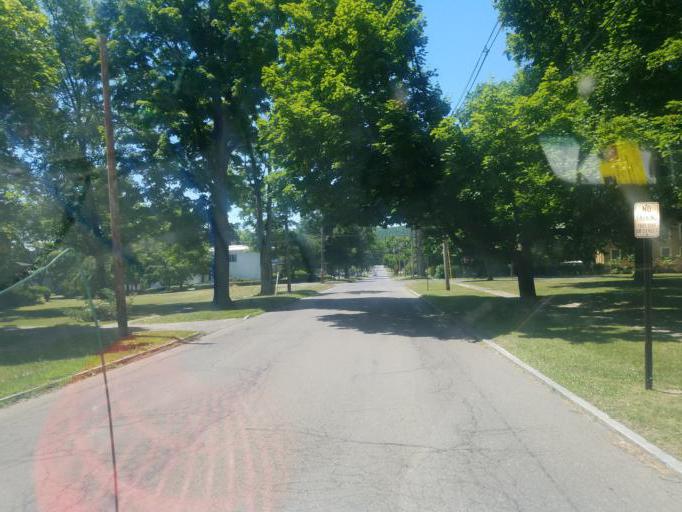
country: US
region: New York
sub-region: Yates County
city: Penn Yan
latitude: 42.6663
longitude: -77.0490
